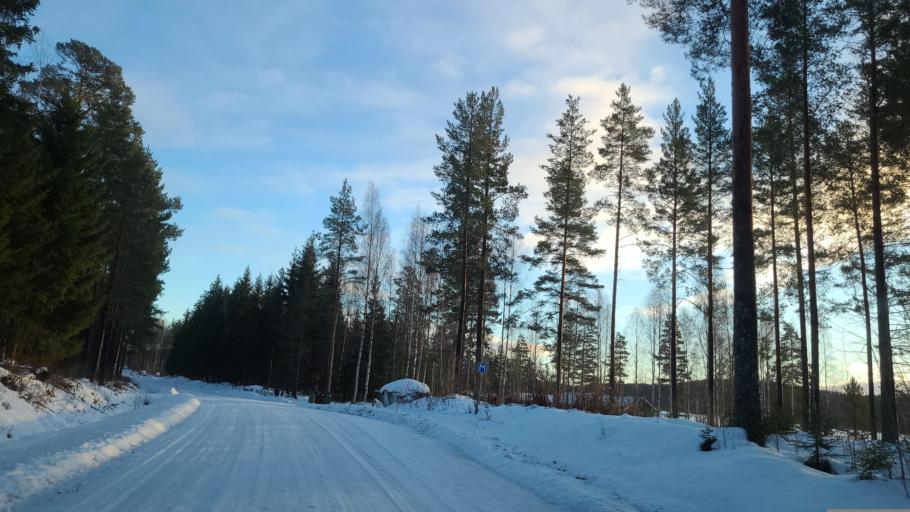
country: SE
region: Gaevleborg
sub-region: Bollnas Kommun
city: Kilafors
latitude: 61.4004
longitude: 16.6487
